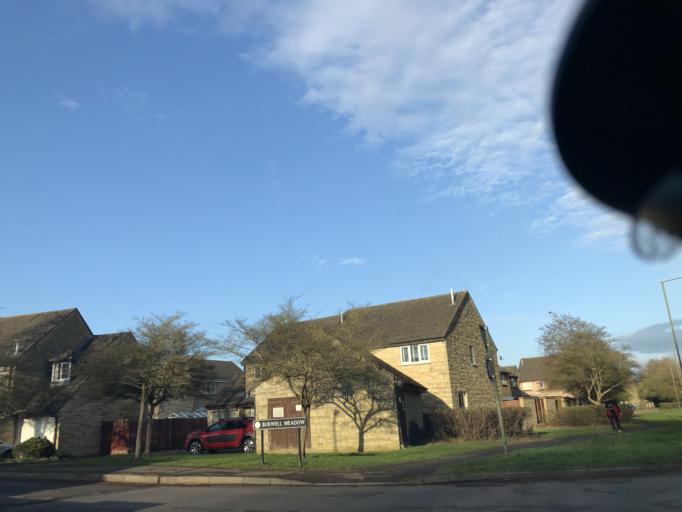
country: GB
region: England
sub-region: Oxfordshire
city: Witney
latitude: 51.7762
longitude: -1.4995
